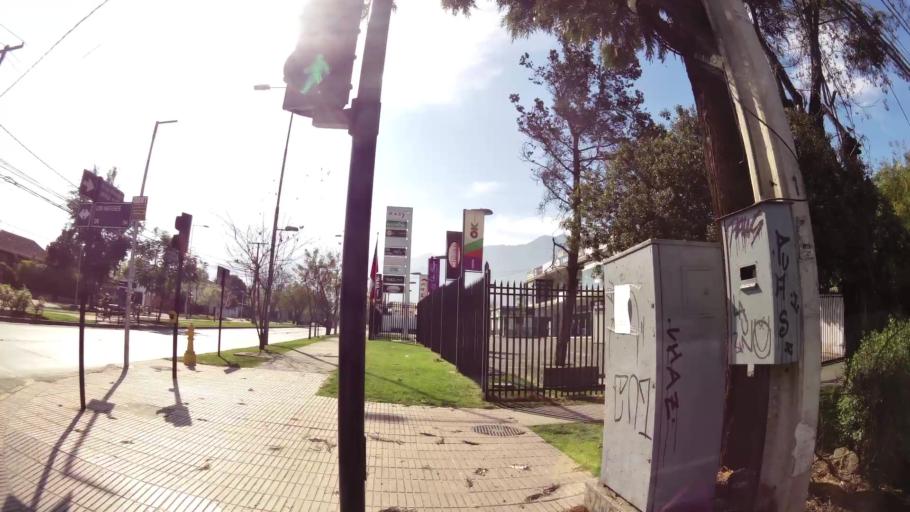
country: CL
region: Santiago Metropolitan
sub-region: Provincia de Santiago
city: Villa Presidente Frei, Nunoa, Santiago, Chile
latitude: -33.4519
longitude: -70.5554
